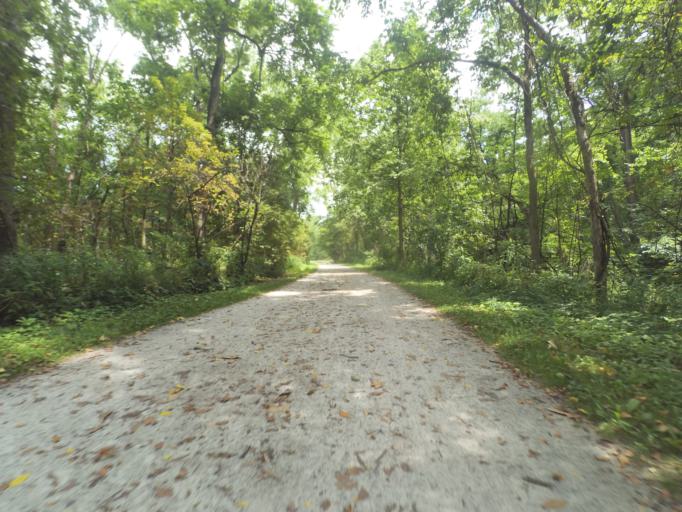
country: US
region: Ohio
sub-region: Summit County
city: Peninsula
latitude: 41.2506
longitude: -81.5467
